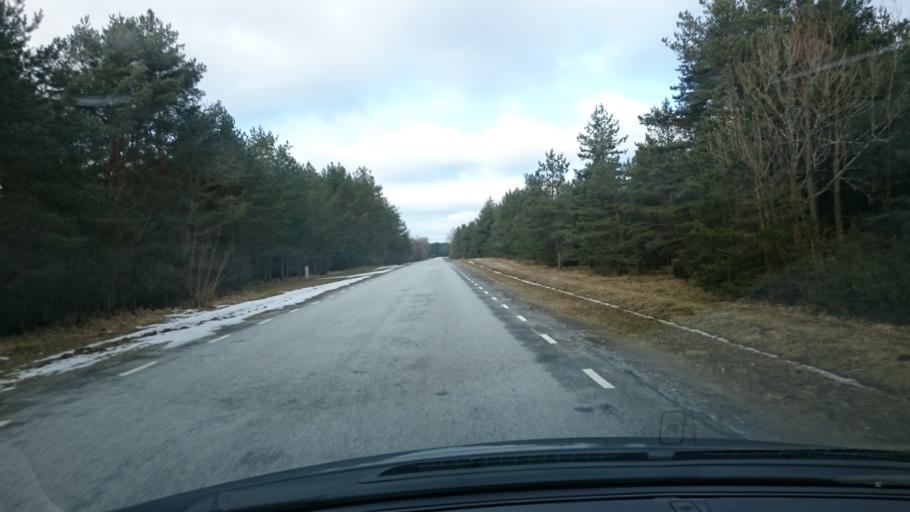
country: EE
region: Harju
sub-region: Keila linn
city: Keila
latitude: 59.3523
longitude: 24.3483
